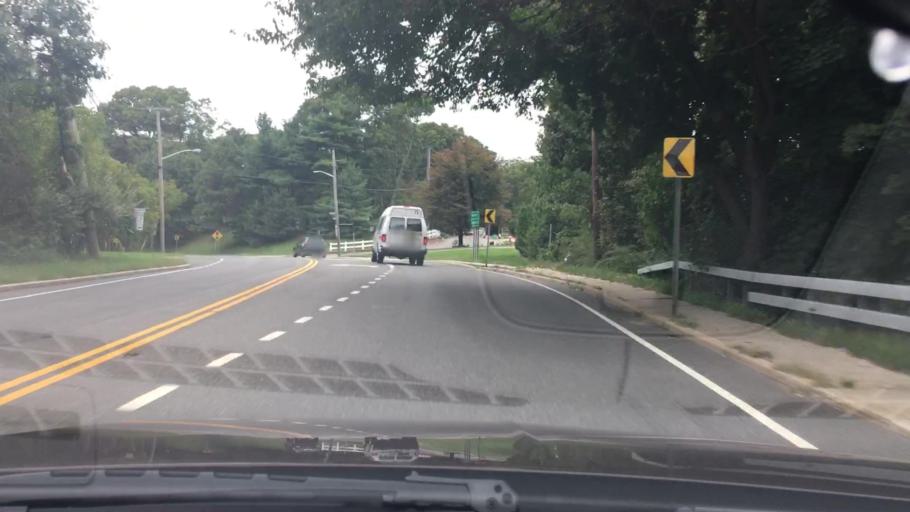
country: US
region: New York
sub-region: Nassau County
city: Bethpage
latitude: 40.7356
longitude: -73.4702
